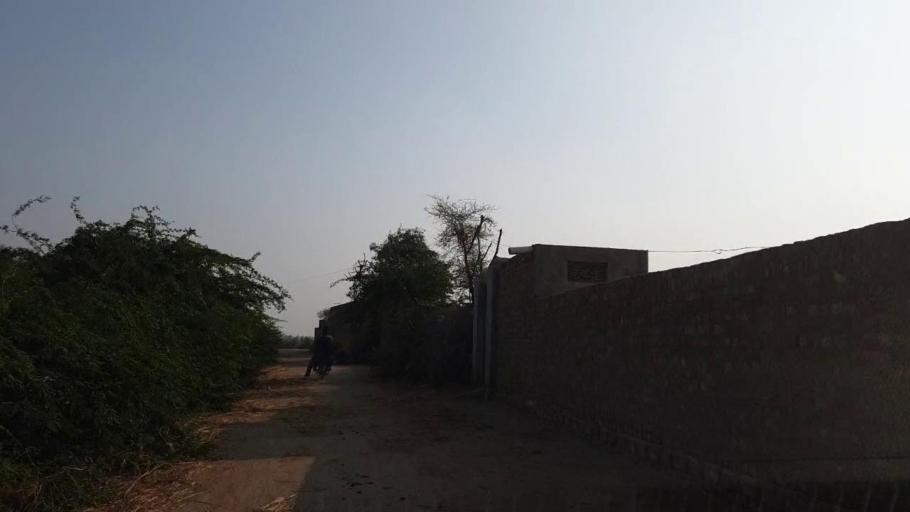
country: PK
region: Sindh
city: Kario
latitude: 24.9260
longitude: 68.5635
